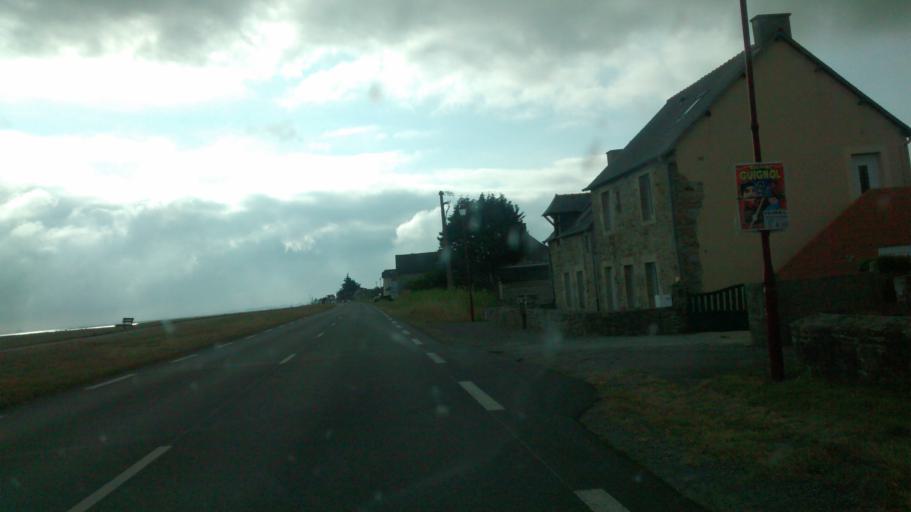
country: FR
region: Brittany
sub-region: Departement d'Ille-et-Vilaine
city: Hirel
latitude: 48.6085
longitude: -1.8154
